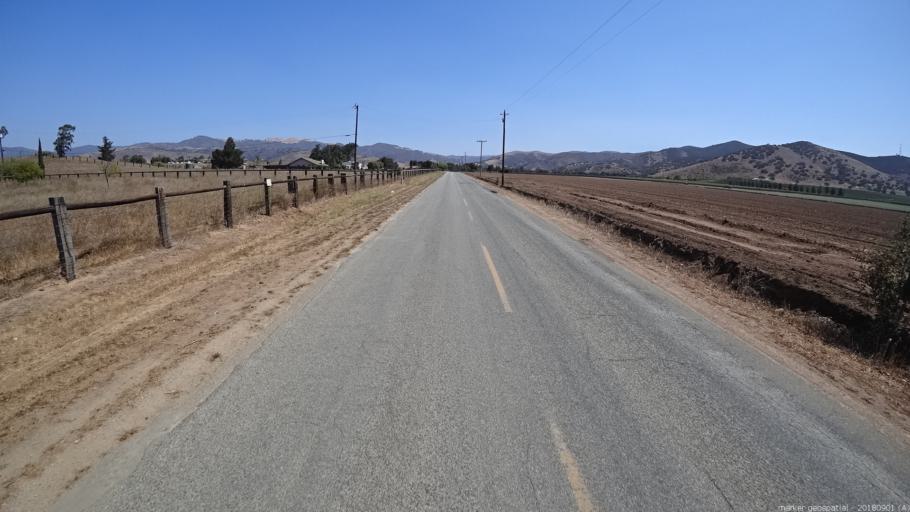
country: US
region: California
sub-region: Monterey County
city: Chualar
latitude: 36.5887
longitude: -121.4613
